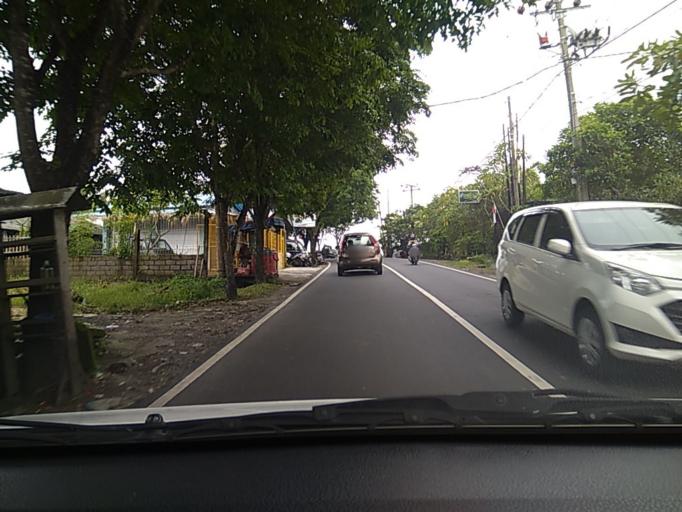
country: ID
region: Bali
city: Banjar Gunungpande
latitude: -8.6363
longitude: 115.1447
